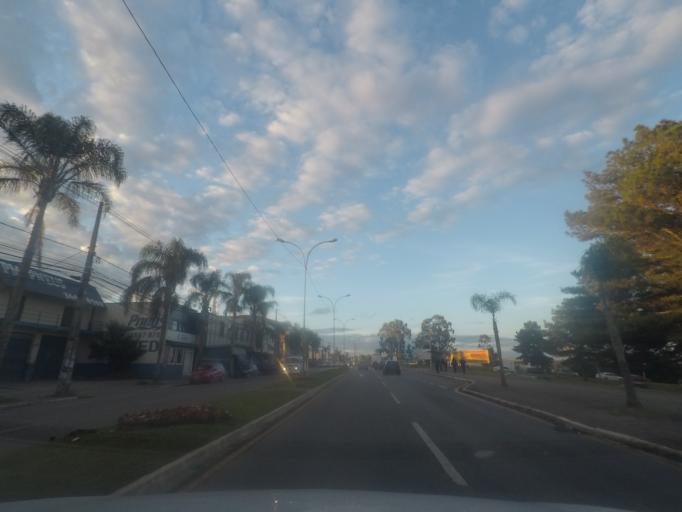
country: BR
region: Parana
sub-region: Pinhais
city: Pinhais
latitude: -25.4385
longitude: -49.1864
